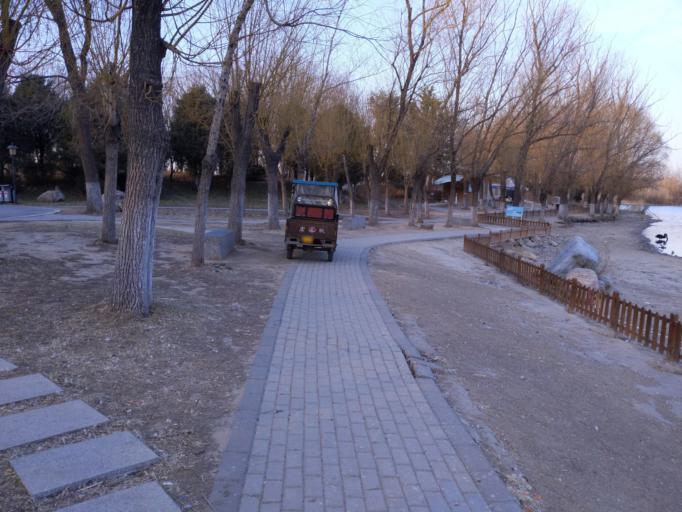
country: CN
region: Henan Sheng
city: Puyang
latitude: 35.7837
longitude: 114.9512
